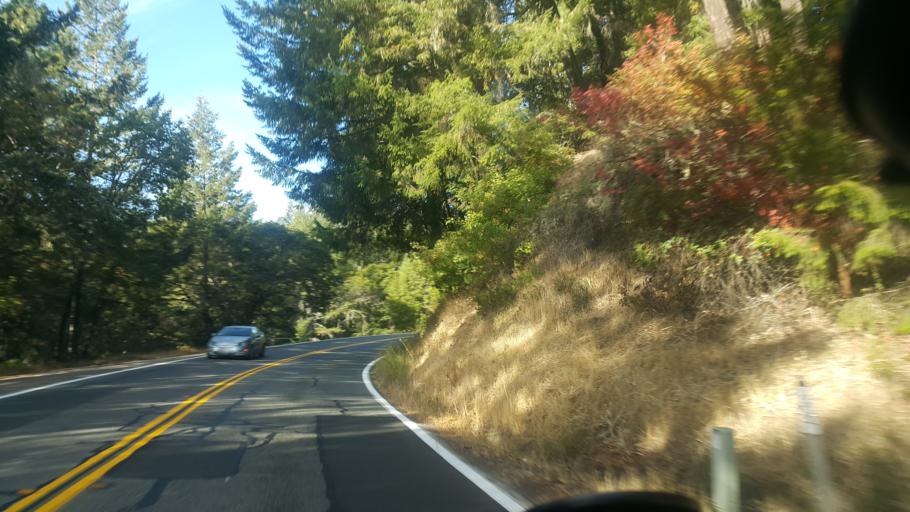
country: US
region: California
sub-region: Mendocino County
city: Brooktrails
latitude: 39.3883
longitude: -123.4237
